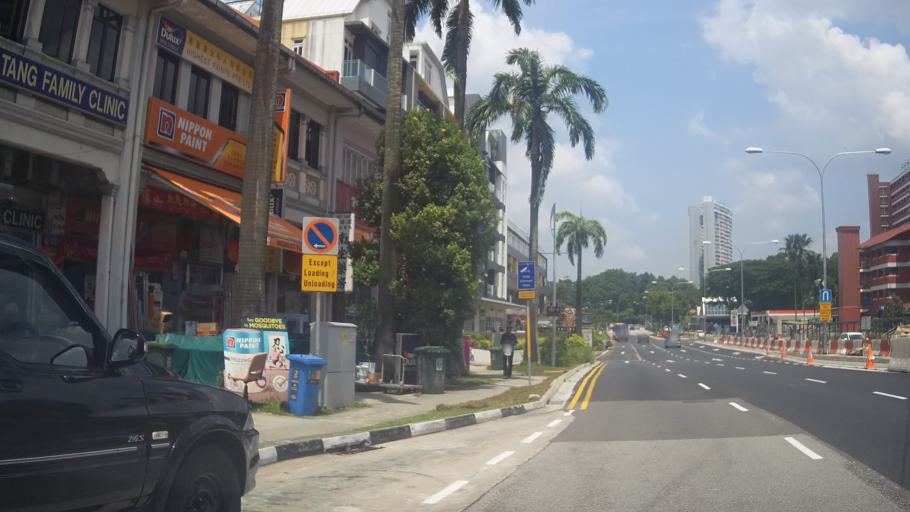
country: SG
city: Singapore
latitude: 1.3396
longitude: 103.7735
